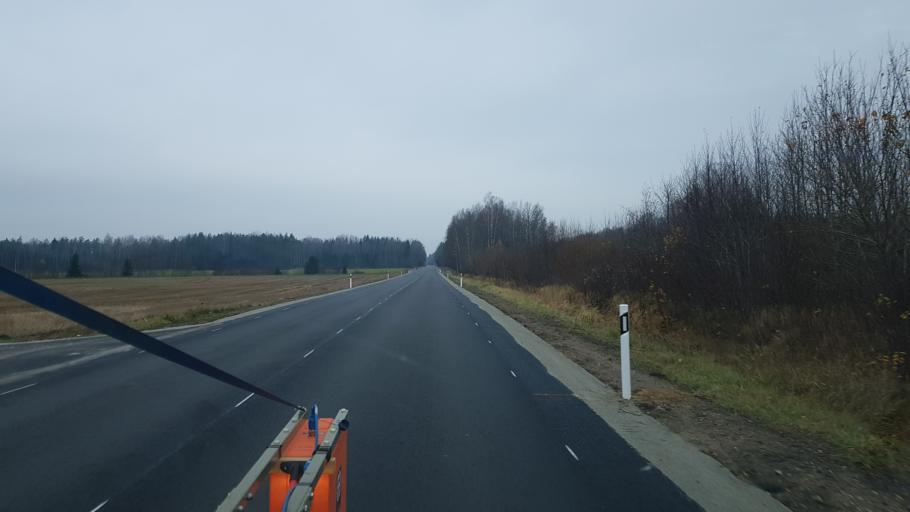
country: EE
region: Paernumaa
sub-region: Vaendra vald (alev)
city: Vandra
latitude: 58.8401
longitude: 25.0674
